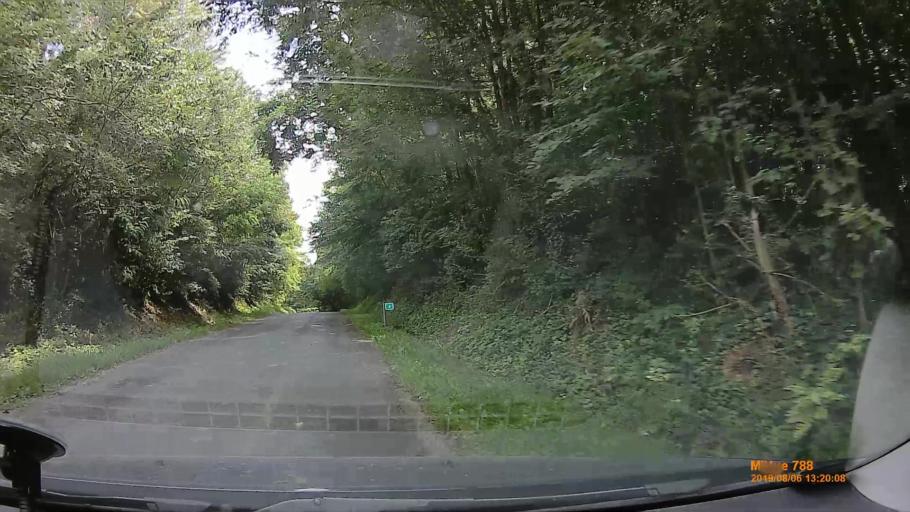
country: HU
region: Zala
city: Pacsa
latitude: 46.6374
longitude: 17.0734
